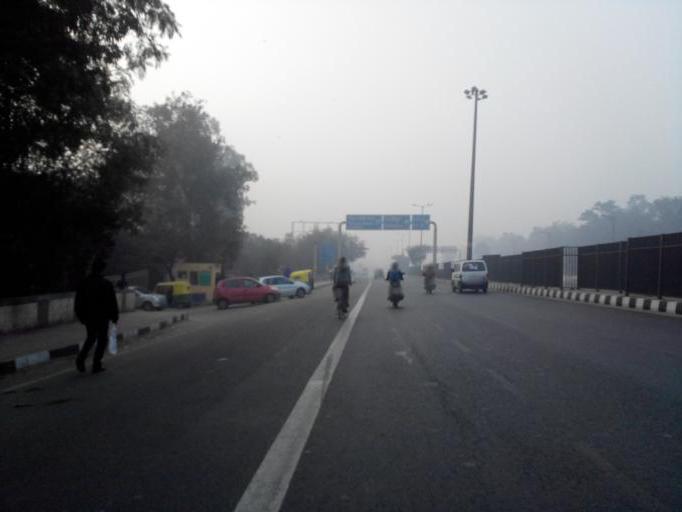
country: IN
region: Uttar Pradesh
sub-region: Gautam Buddha Nagar
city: Noida
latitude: 28.6599
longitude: 77.3201
